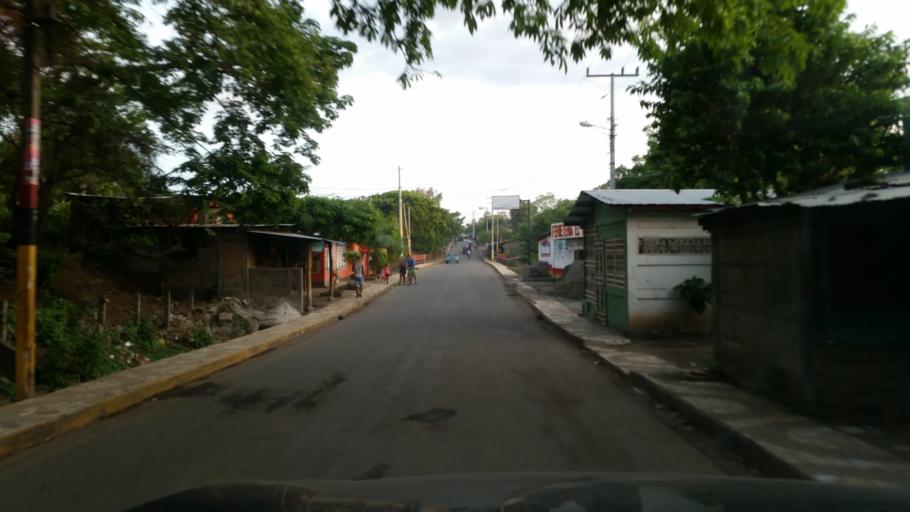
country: NI
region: Managua
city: Masachapa
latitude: 11.7834
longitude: -86.5143
